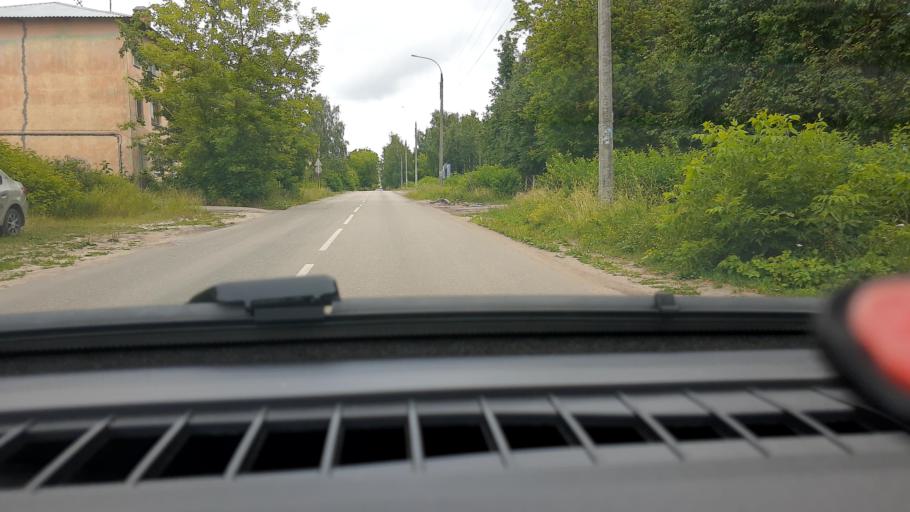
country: RU
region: Nizjnij Novgorod
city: Dzerzhinsk
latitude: 56.2420
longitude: 43.4271
